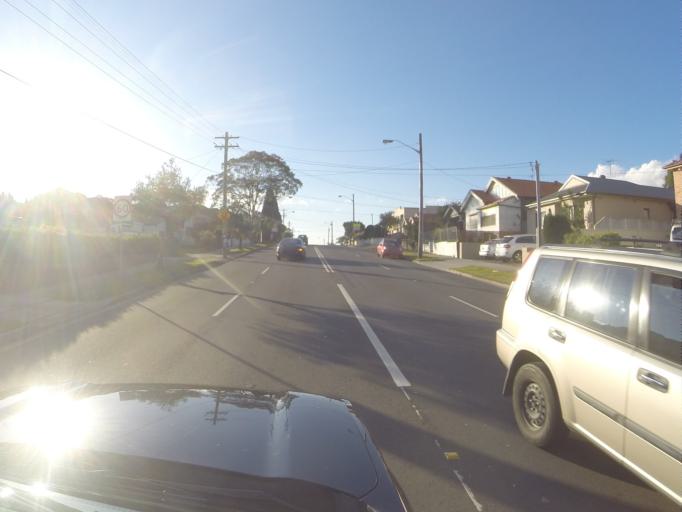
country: AU
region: New South Wales
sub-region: Rockdale
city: Bexley North
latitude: -33.9316
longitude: 151.1098
